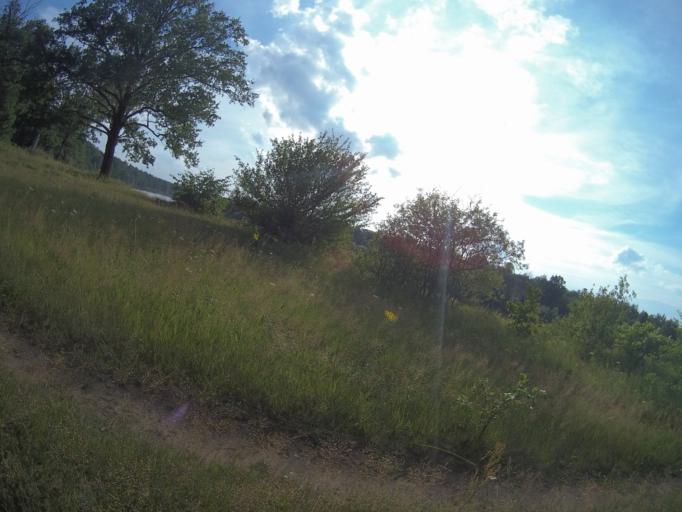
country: RU
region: Vladimir
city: Vorsha
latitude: 56.0105
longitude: 40.0916
